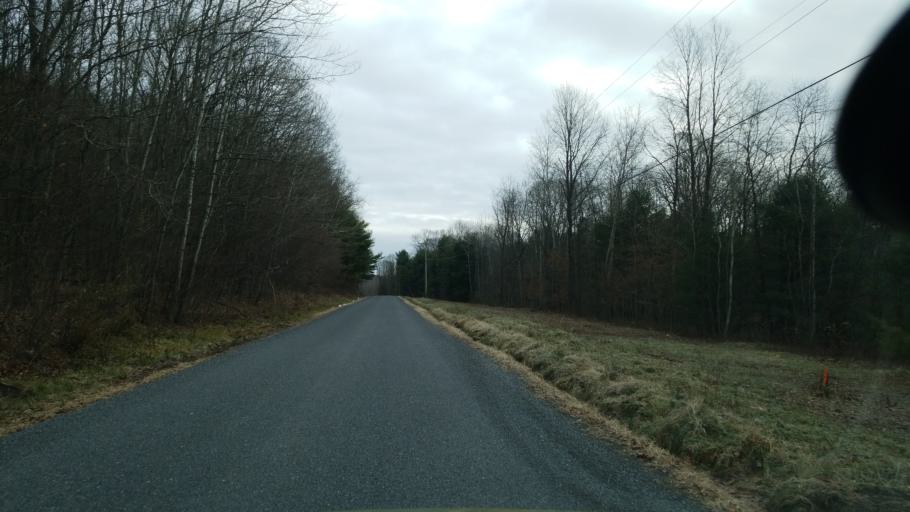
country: US
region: Pennsylvania
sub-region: Clearfield County
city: Treasure Lake
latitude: 41.1406
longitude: -78.5966
